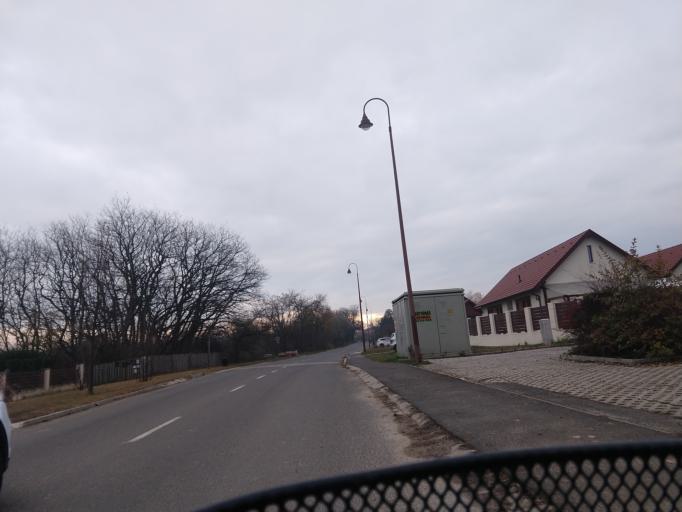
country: HU
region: Pest
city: Orbottyan
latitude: 47.6658
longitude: 19.2620
